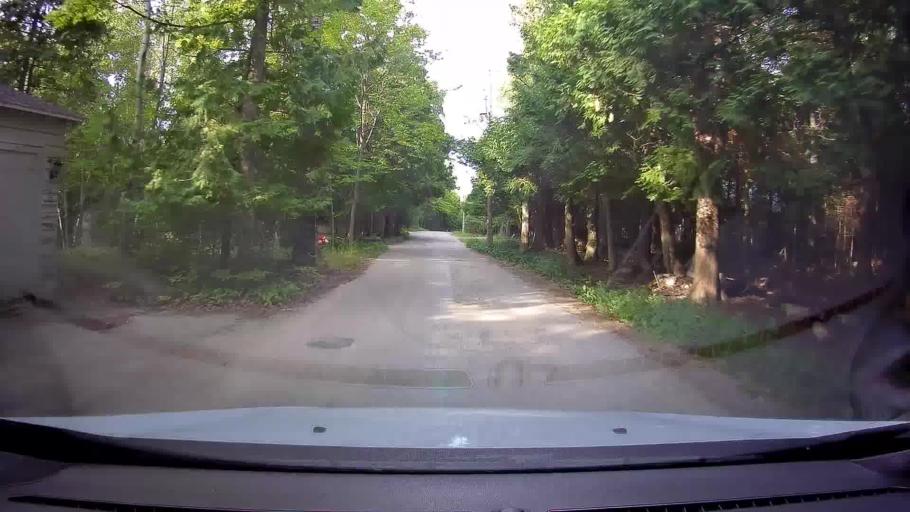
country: US
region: Wisconsin
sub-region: Door County
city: Sturgeon Bay
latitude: 45.1899
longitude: -87.1472
